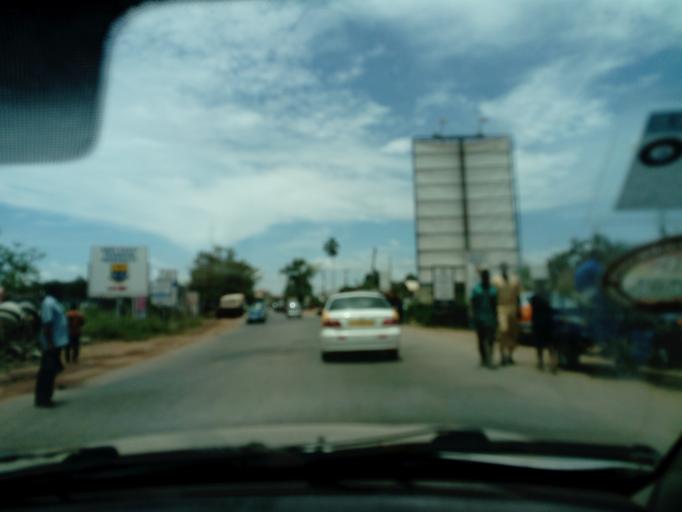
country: GH
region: Central
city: Cape Coast
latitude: 5.1364
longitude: -1.2785
